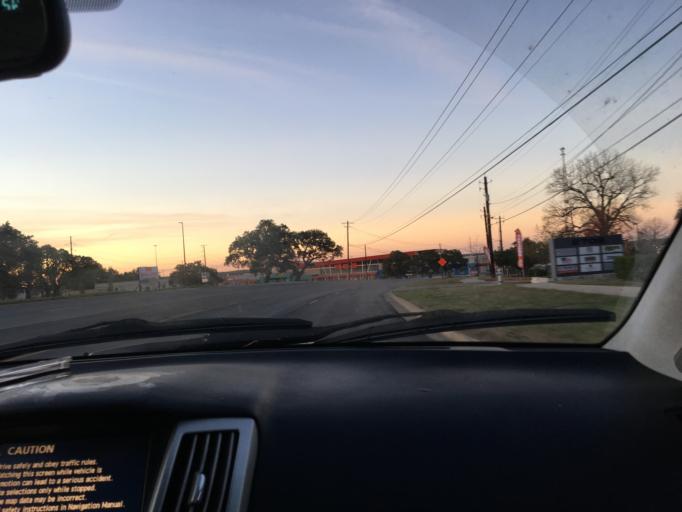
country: US
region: Texas
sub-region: Travis County
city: Onion Creek
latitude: 30.1717
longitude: -97.7858
